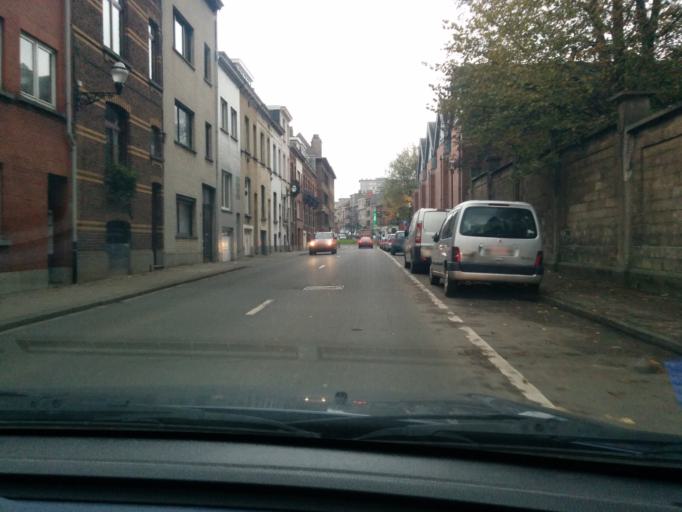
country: BE
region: Flanders
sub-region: Provincie Vlaams-Brabant
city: Wemmel
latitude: 50.8851
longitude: 4.3281
